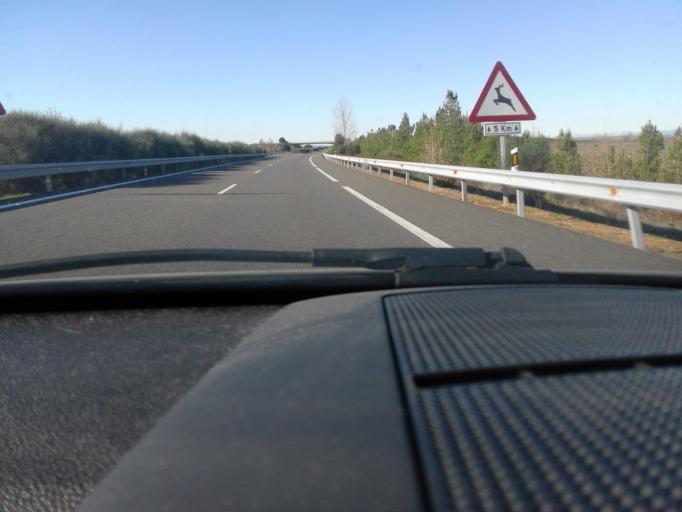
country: ES
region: Castille and Leon
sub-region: Provincia de Leon
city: Villanueva de las Manzanas
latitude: 42.4578
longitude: -5.4480
